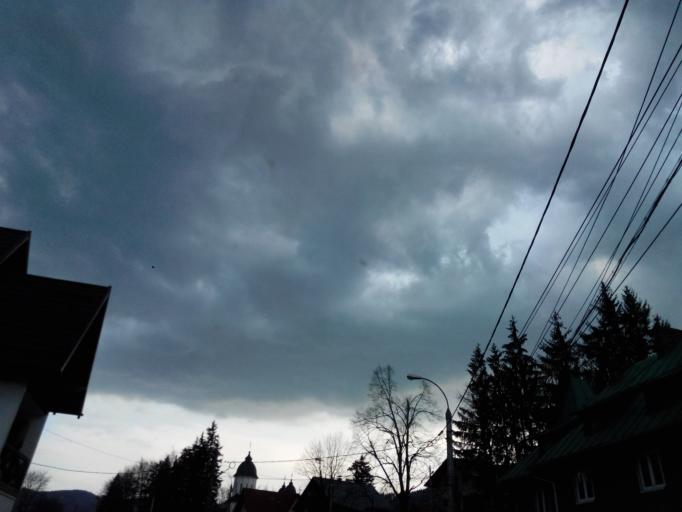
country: RO
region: Prahova
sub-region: Oras Sinaia
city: Sinaia
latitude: 45.3278
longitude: 25.5639
